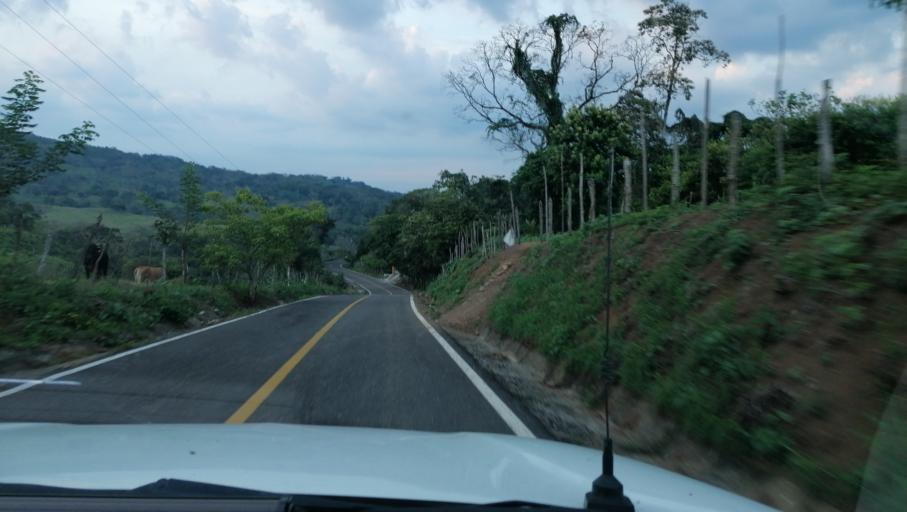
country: MX
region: Chiapas
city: Pichucalco
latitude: 17.5258
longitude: -93.1541
